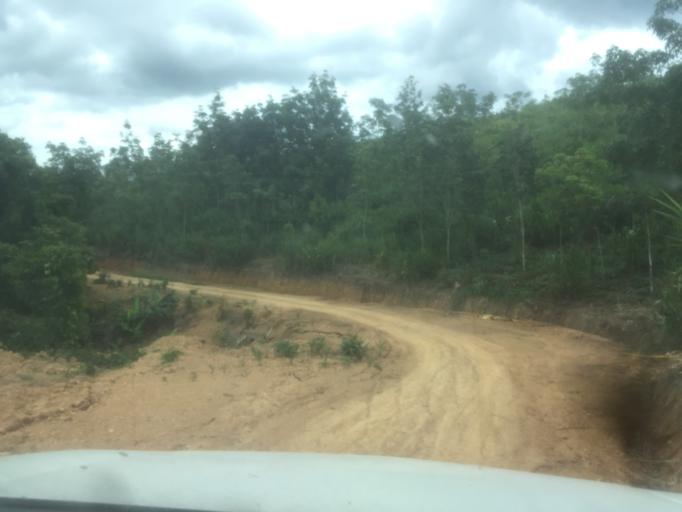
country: LA
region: Phongsali
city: Khoa
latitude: 20.9258
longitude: 102.5448
